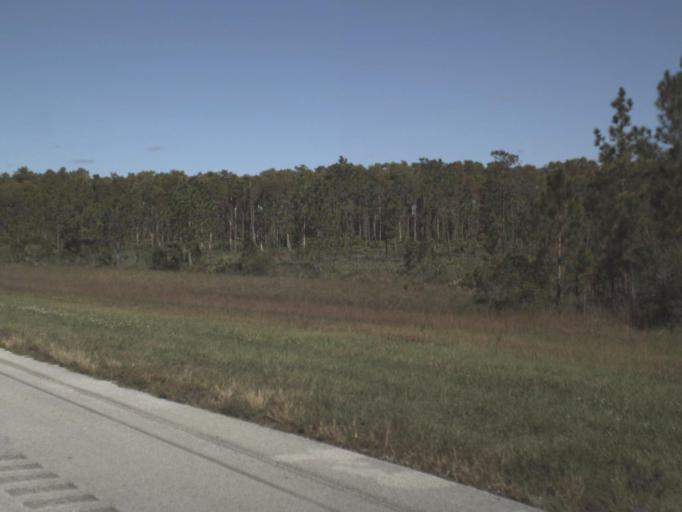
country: US
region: Florida
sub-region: Osceola County
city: Saint Cloud
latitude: 27.9991
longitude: -81.1366
